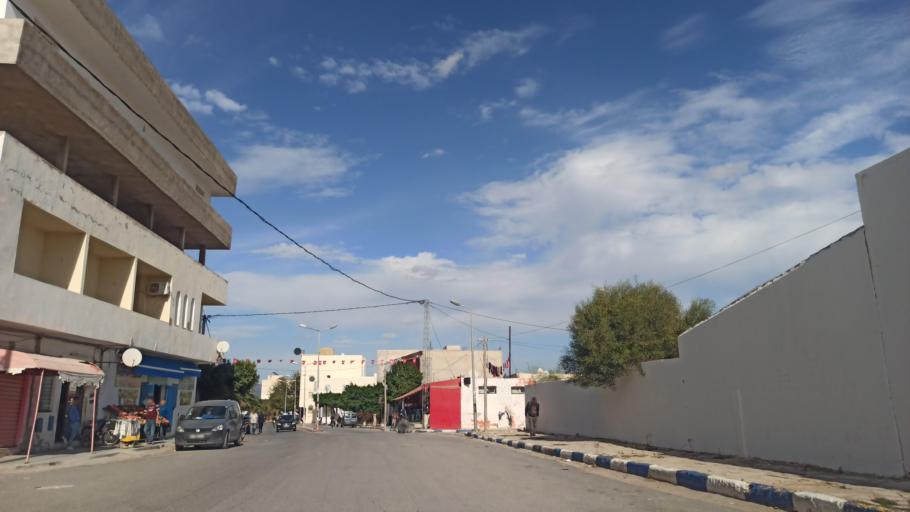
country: TN
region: Zaghwan
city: Zaghouan
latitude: 36.3510
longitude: 10.2075
